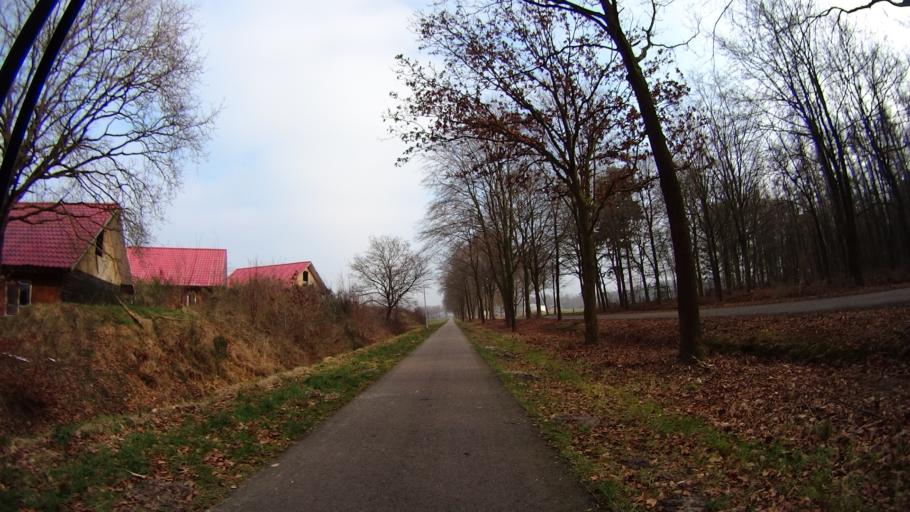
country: NL
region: Drenthe
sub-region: Gemeente Coevorden
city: Sleen
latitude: 52.7445
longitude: 6.8064
